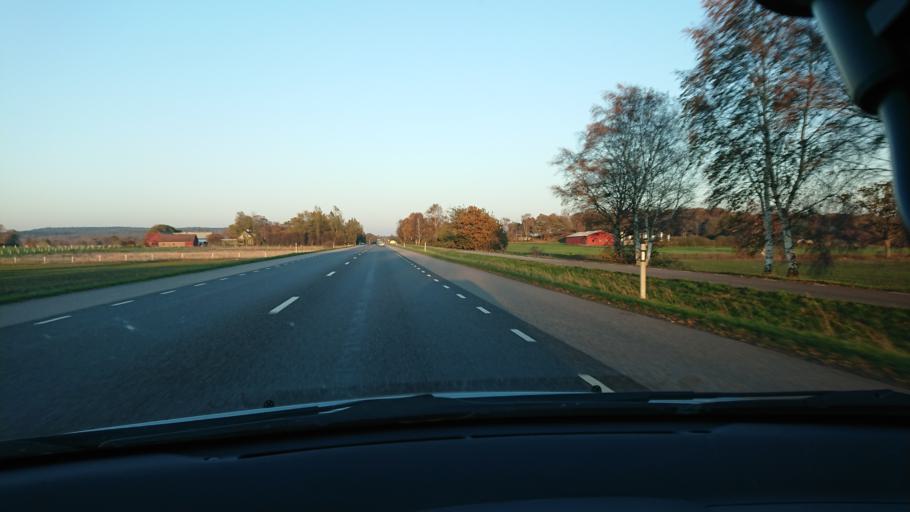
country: SE
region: Halland
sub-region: Halmstads Kommun
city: Fyllinge
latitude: 56.6890
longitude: 12.9603
